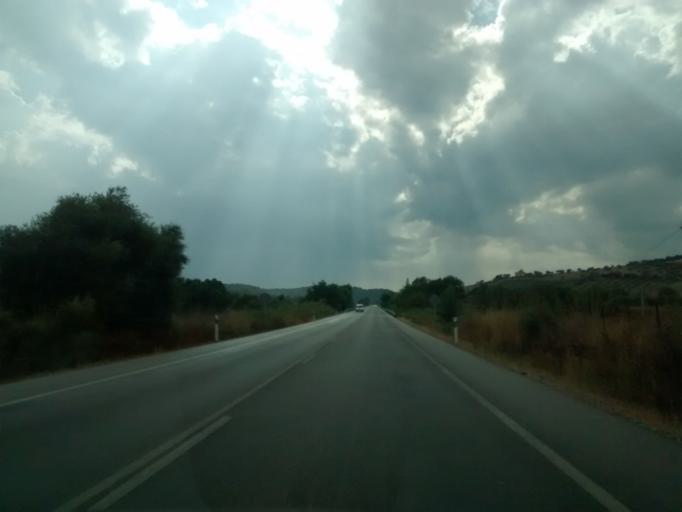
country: ES
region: Andalusia
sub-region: Provincia de Cadiz
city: Prado del Rey
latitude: 36.7529
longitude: -5.5583
